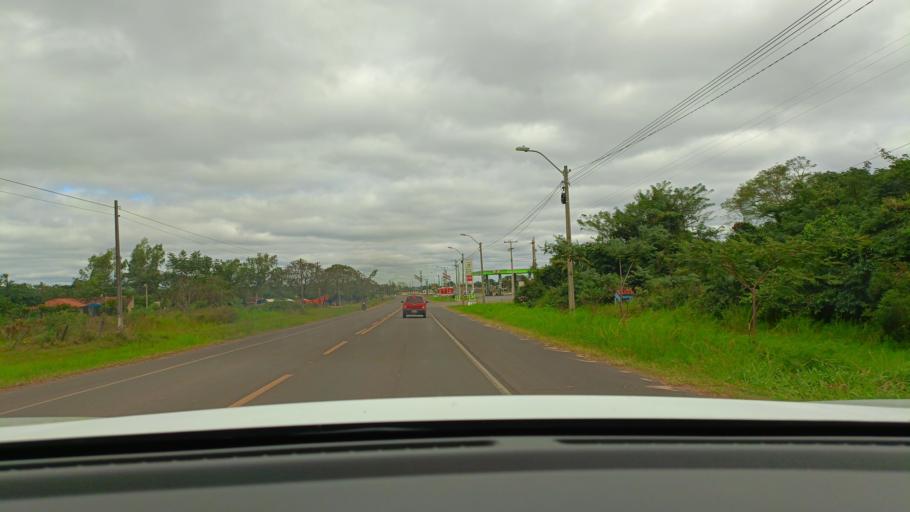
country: PY
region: San Pedro
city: Union
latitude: -24.6808
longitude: -56.4661
